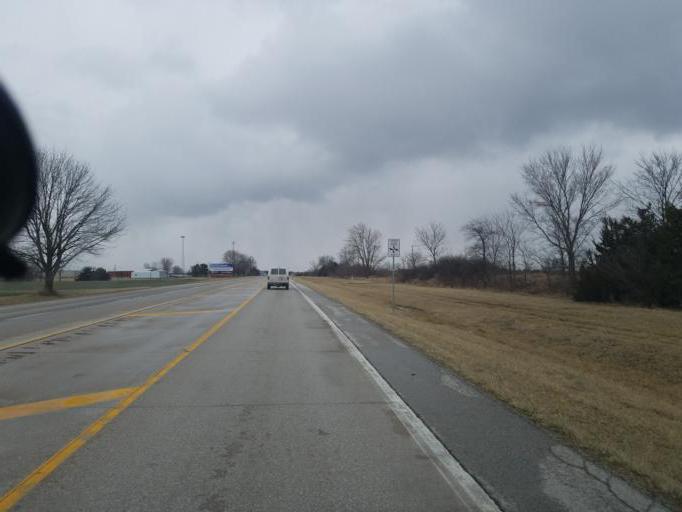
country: US
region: Missouri
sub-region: Macon County
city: Macon
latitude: 39.7717
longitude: -92.4734
